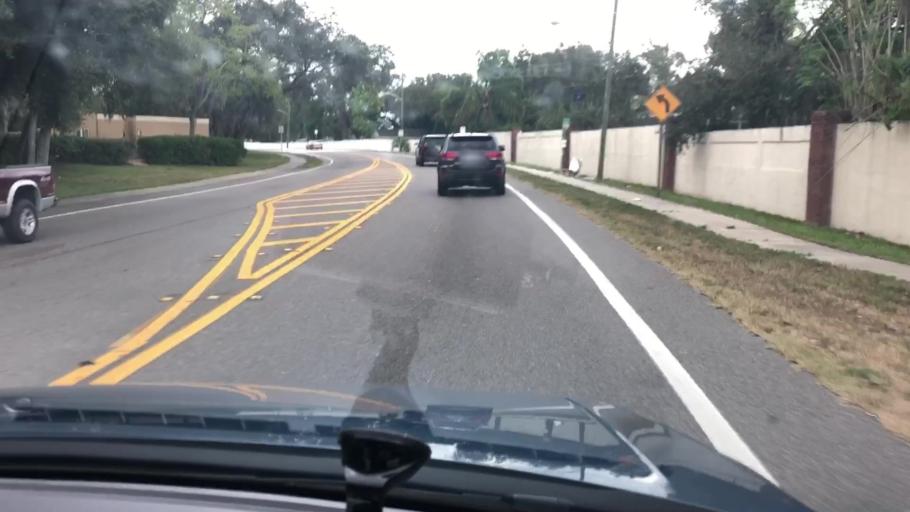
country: US
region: Florida
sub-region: Polk County
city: Gibsonia
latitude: 28.1077
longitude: -81.9381
